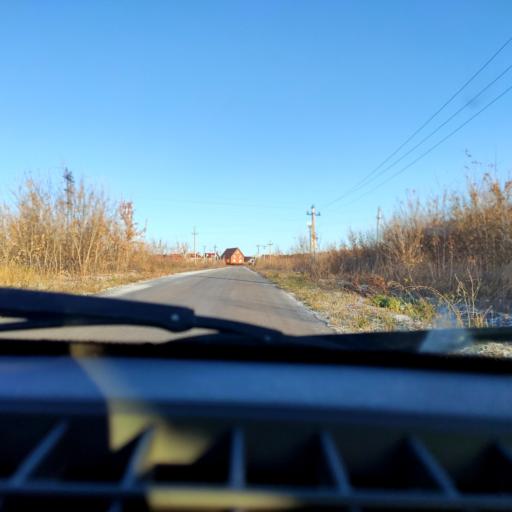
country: RU
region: Bashkortostan
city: Avdon
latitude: 54.6536
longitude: 55.7516
